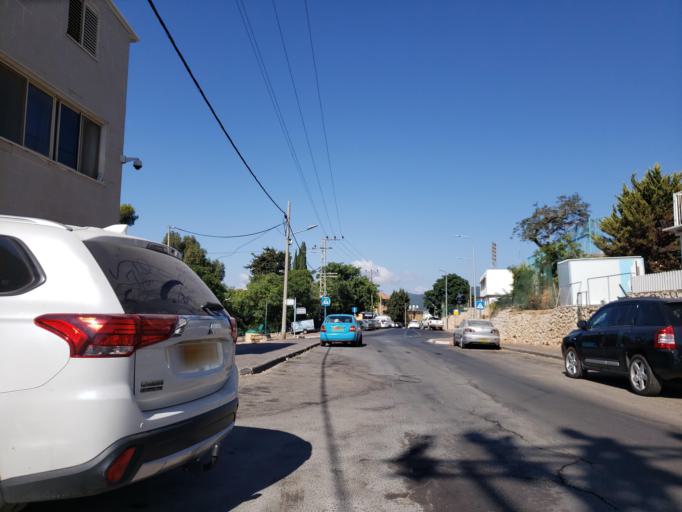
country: IL
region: Northern District
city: Safed
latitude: 32.9562
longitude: 35.4986
